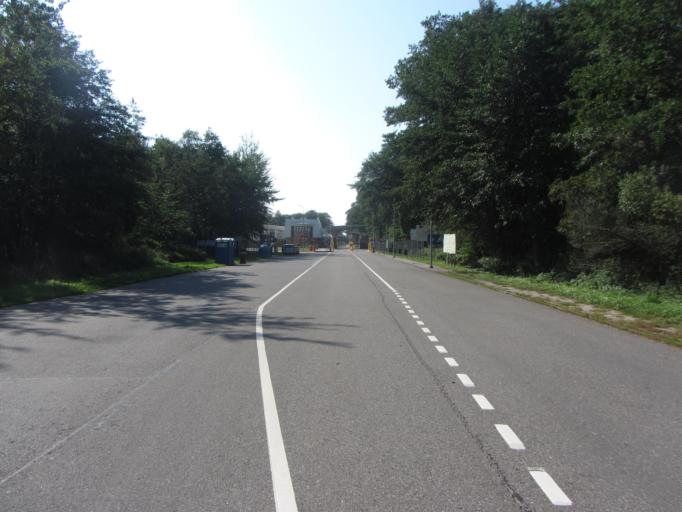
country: LT
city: Nida
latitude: 55.2821
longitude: 20.9666
